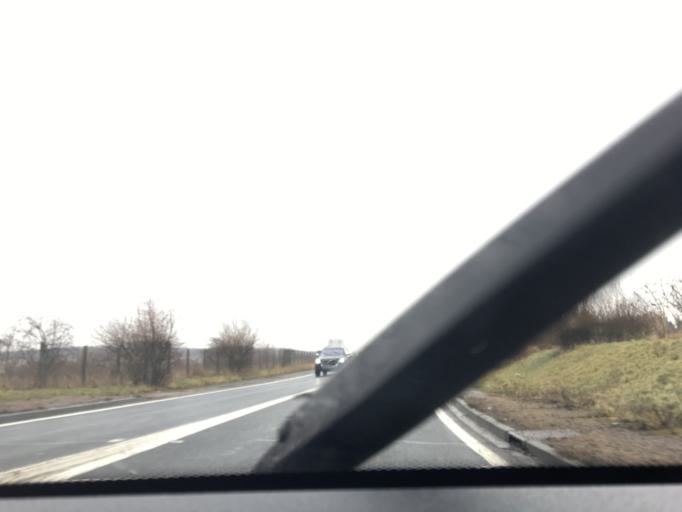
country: FR
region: Ile-de-France
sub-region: Departement des Yvelines
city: Limay
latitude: 49.0055
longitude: 1.7413
